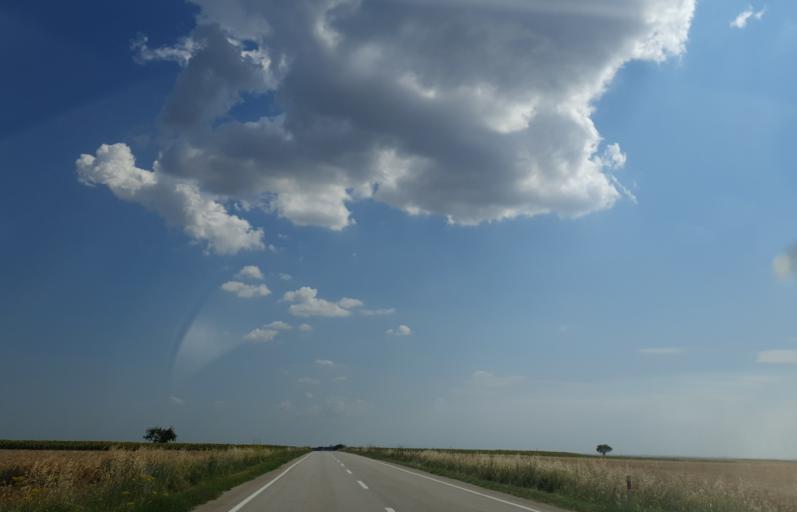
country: TR
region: Kirklareli
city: Buyukkaristiran
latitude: 41.4043
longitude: 27.5755
